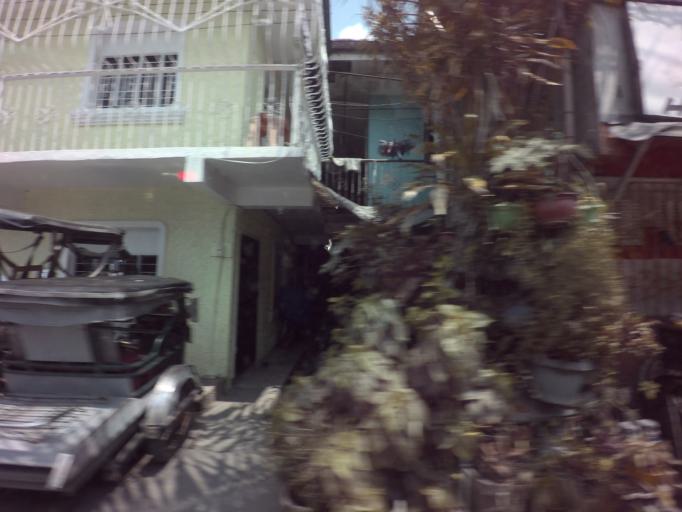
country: PH
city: Sambayanihan People's Village
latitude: 14.4403
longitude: 121.0506
